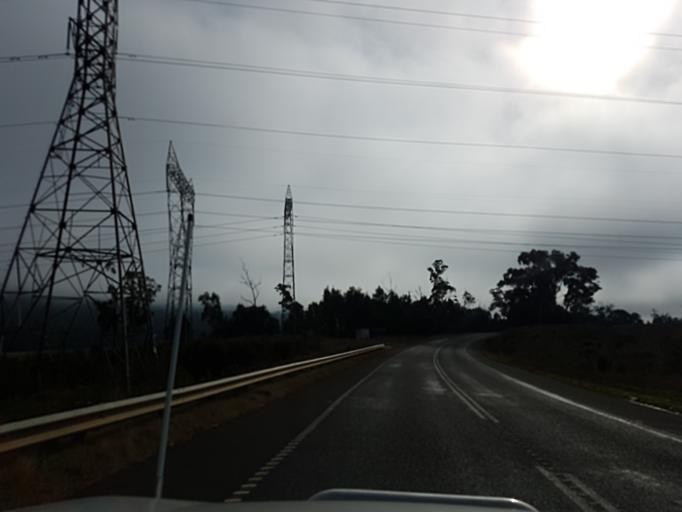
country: AU
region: Victoria
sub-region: Murrindindi
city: Kinglake West
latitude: -37.4512
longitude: 145.4175
